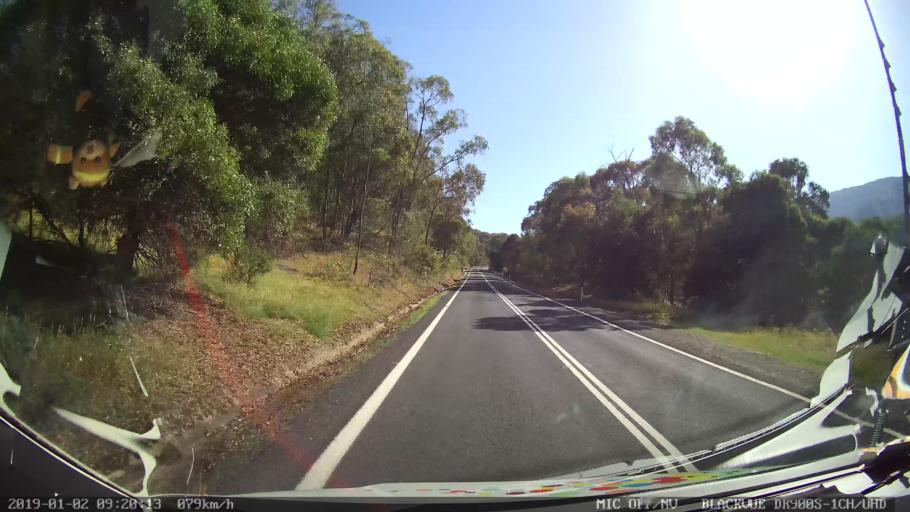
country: AU
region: New South Wales
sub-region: Tumut Shire
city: Tumut
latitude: -35.4142
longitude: 148.2813
